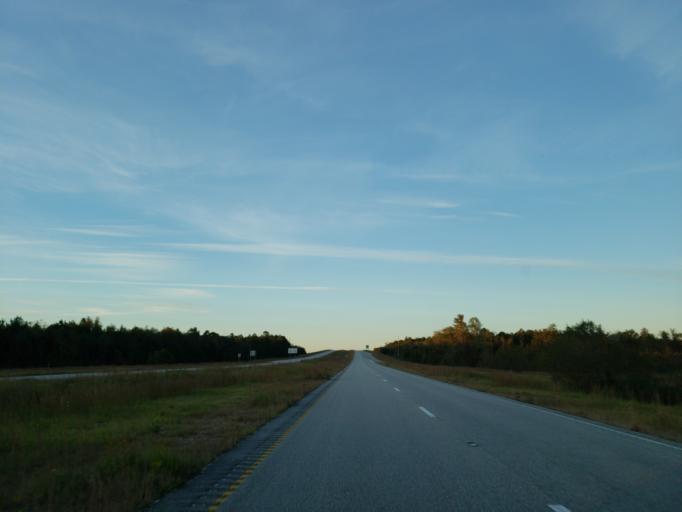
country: US
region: Mississippi
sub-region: Wayne County
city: Belmont
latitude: 31.4382
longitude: -88.4654
